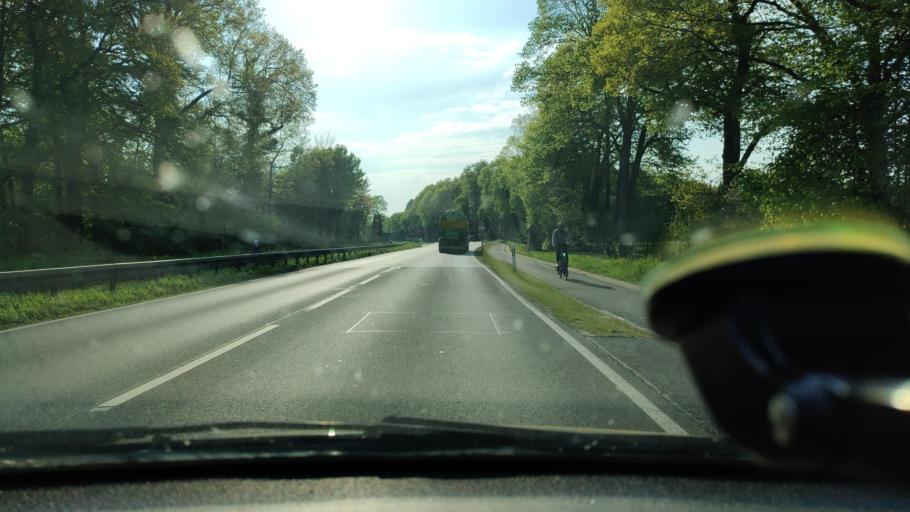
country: DE
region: North Rhine-Westphalia
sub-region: Regierungsbezirk Munster
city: Telgte
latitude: 51.9811
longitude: 7.7506
